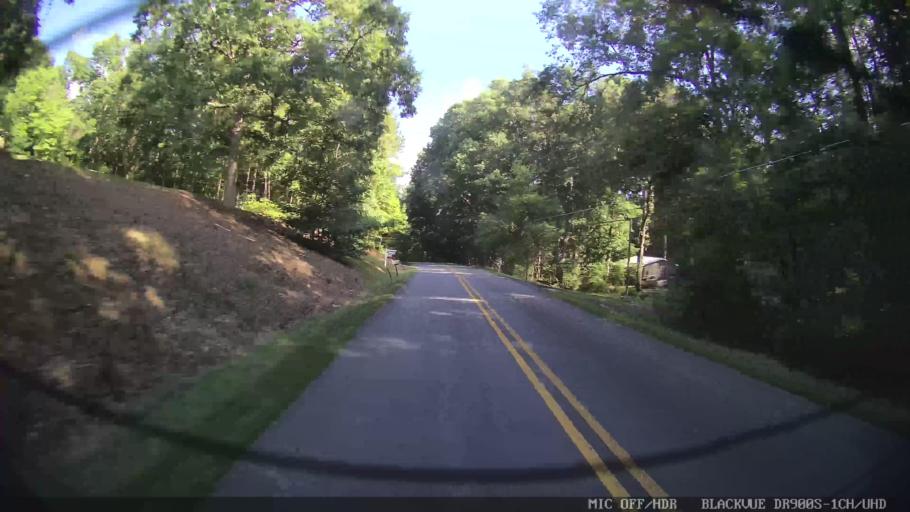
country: US
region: Georgia
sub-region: Floyd County
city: Rome
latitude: 34.2237
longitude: -85.1375
